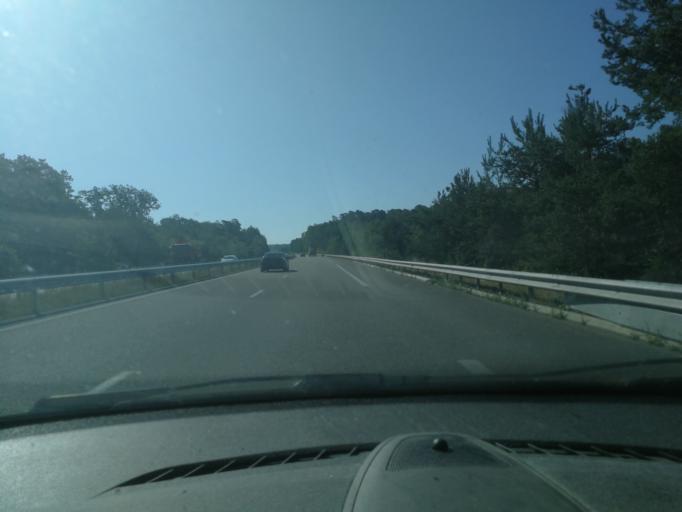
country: FR
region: Alsace
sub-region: Departement du Bas-Rhin
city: Keskastel
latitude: 48.9654
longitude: 7.0751
